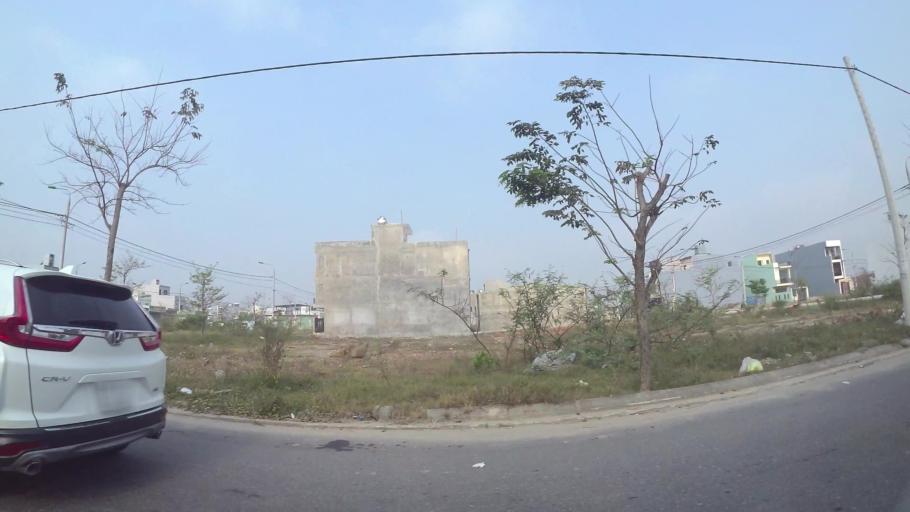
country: VN
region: Da Nang
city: Ngu Hanh Son
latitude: 16.0101
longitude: 108.2293
